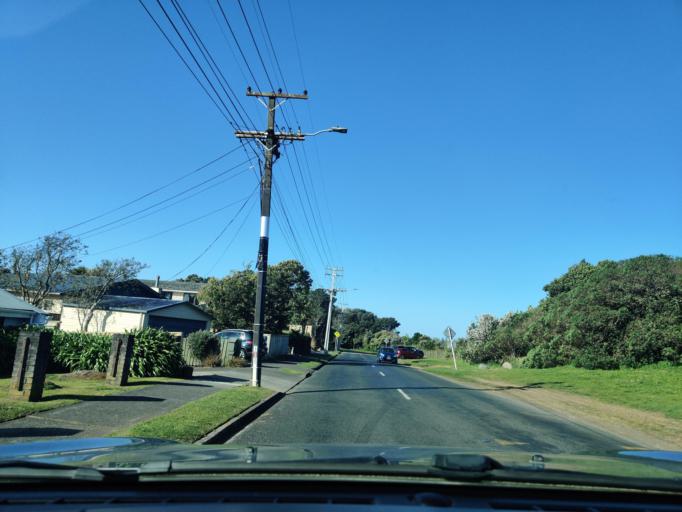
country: NZ
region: Taranaki
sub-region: New Plymouth District
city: New Plymouth
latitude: -39.0463
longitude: 174.1112
